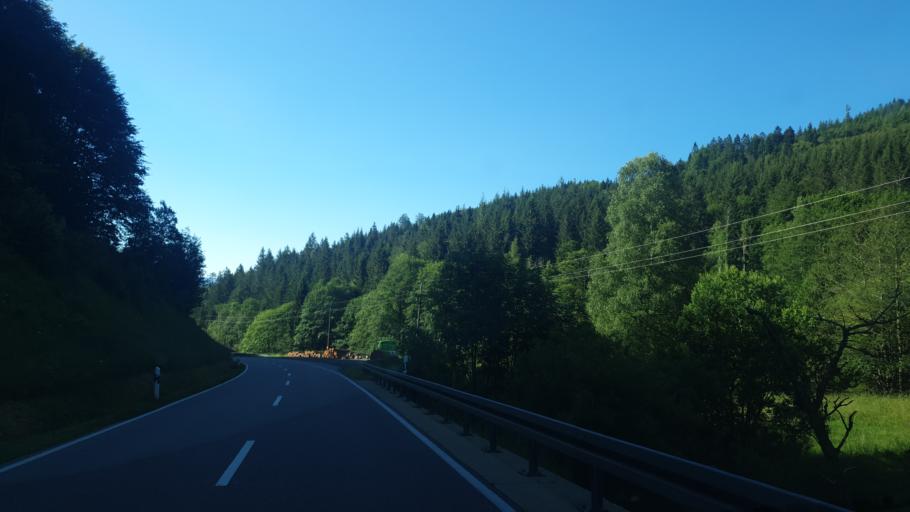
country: DE
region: Baden-Wuerttemberg
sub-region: Freiburg Region
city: Todtnau
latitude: 47.8547
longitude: 7.9178
